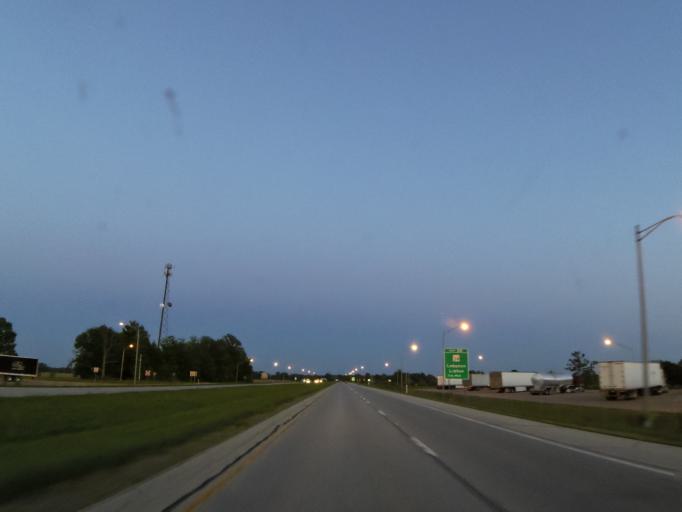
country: US
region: Indiana
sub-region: Hendricks County
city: Pittsboro
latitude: 39.9007
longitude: -86.5548
